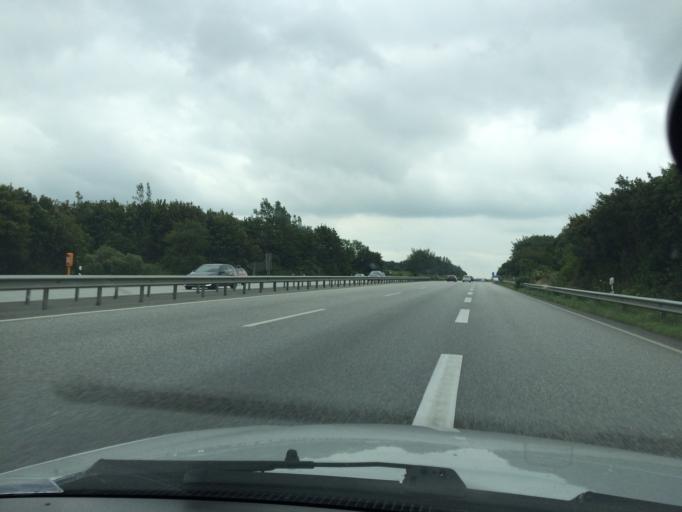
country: DE
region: Schleswig-Holstein
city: Tarp
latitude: 54.6654
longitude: 9.4295
